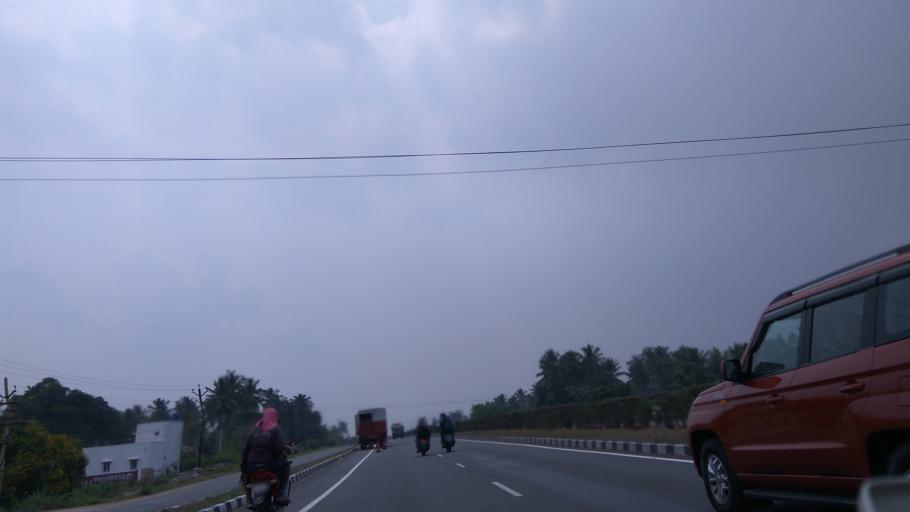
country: IN
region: Tamil Nadu
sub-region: Krishnagiri
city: Kaverippattanam
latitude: 12.4137
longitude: 78.2245
